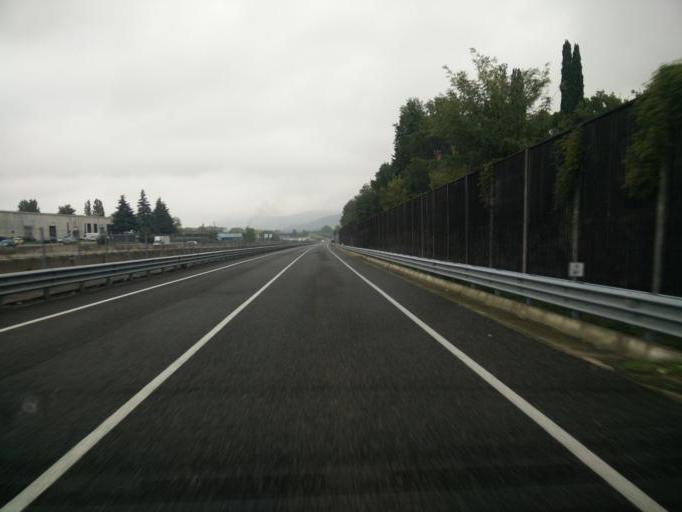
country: IT
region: Emilia-Romagna
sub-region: Provincia di Bologna
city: Borgonuovo
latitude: 44.4236
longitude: 11.2727
